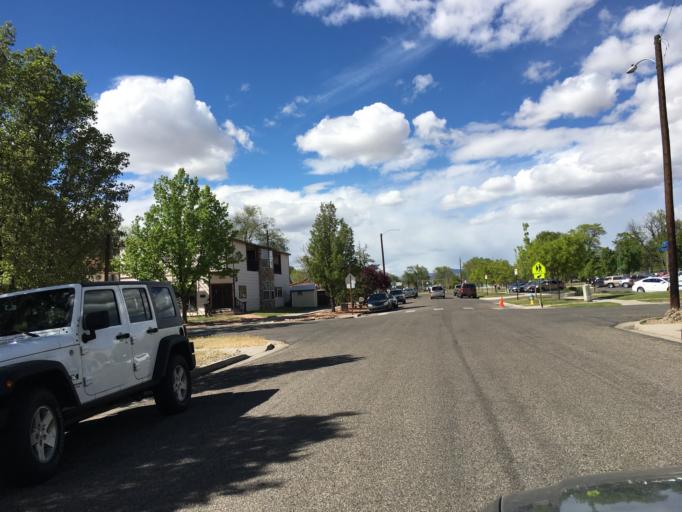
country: US
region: Colorado
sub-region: Mesa County
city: Grand Junction
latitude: 39.0721
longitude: -108.5577
